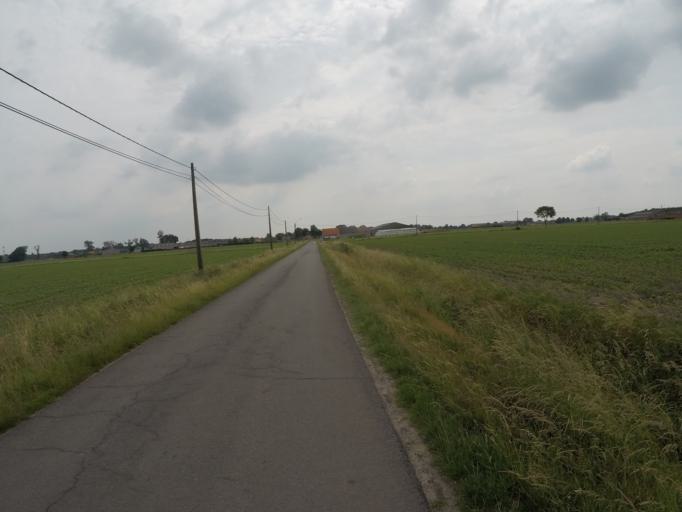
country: BE
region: Flanders
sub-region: Provincie Antwerpen
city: Wuustwezel
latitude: 51.4072
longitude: 4.5902
